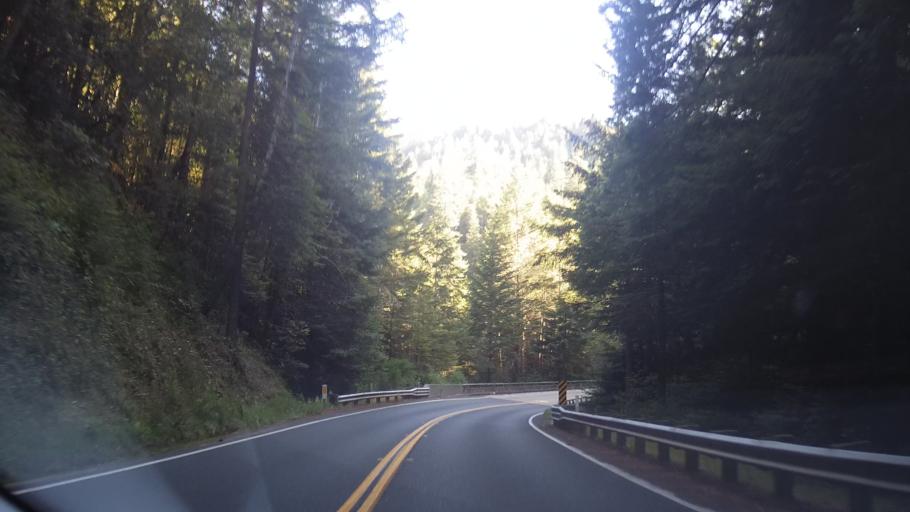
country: US
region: California
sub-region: Mendocino County
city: Brooktrails
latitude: 39.3493
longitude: -123.5114
